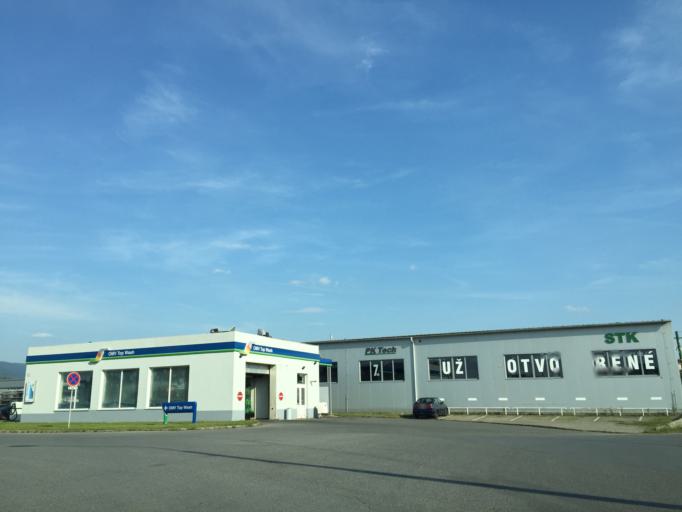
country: SK
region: Presovsky
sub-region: Okres Presov
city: Presov
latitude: 49.0075
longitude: 21.2491
